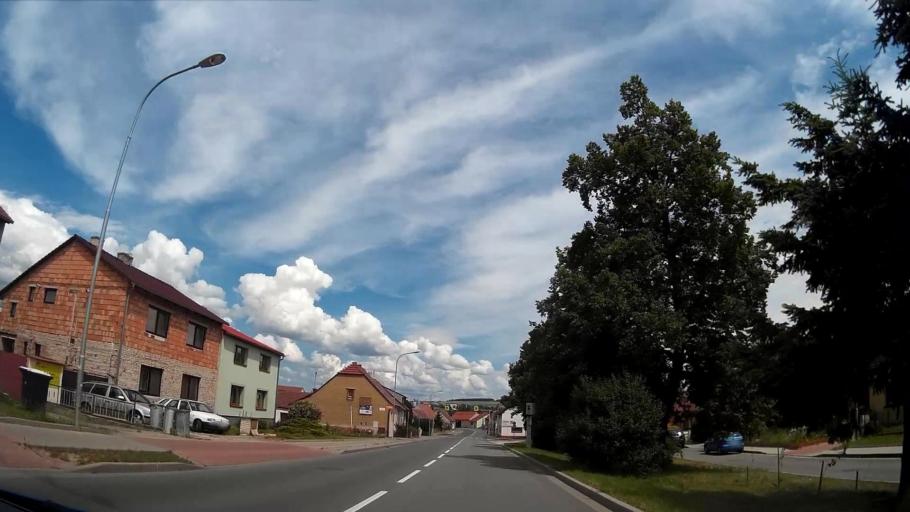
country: CZ
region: South Moravian
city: Ivancice
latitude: 49.0917
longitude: 16.3683
